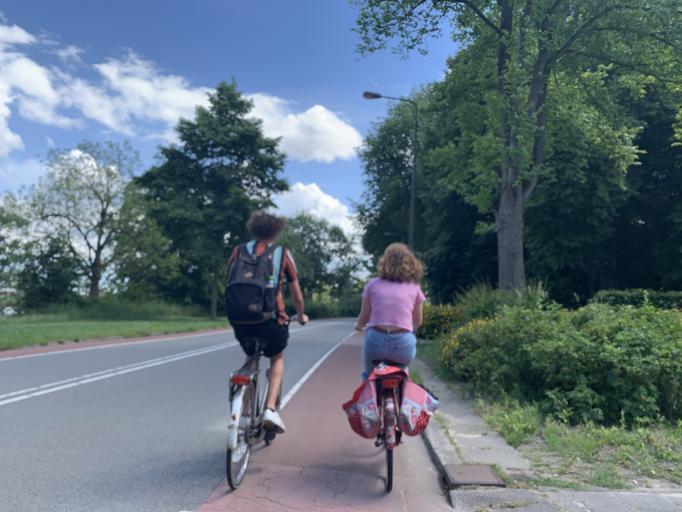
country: NL
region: Groningen
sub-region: Gemeente Groningen
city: Oosterpark
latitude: 53.2023
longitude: 6.5888
